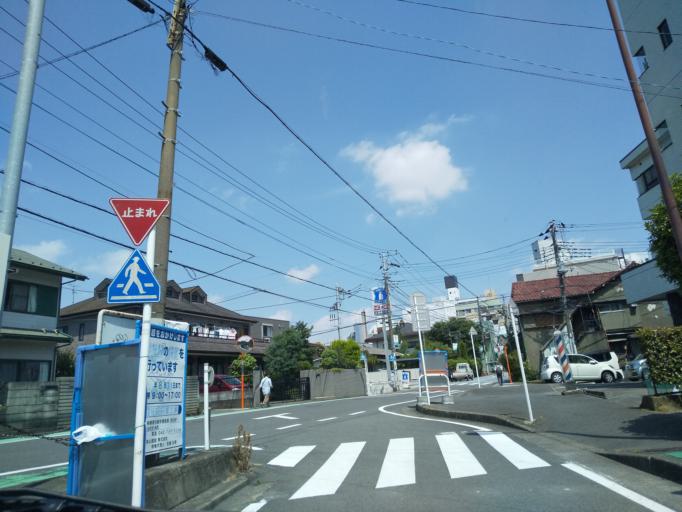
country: JP
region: Kanagawa
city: Zama
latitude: 35.4999
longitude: 139.4053
